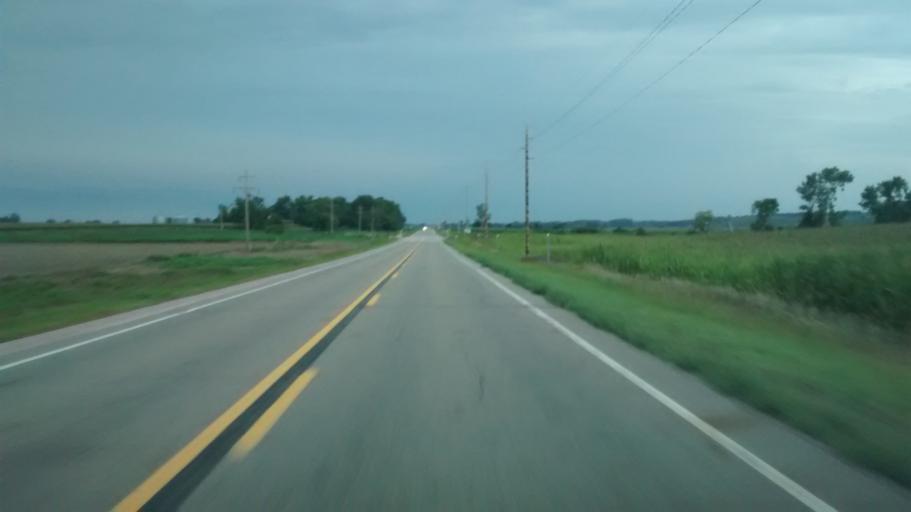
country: US
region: Iowa
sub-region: Woodbury County
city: Moville
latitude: 42.5366
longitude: -96.0322
